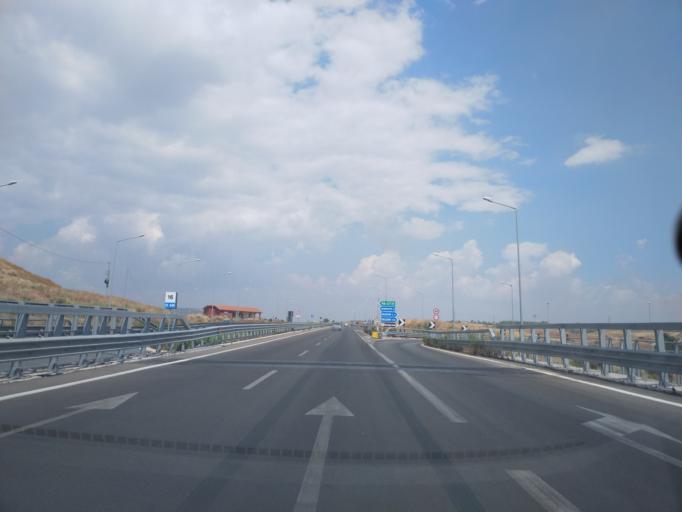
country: IT
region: Sicily
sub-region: Agrigento
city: Favara
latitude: 37.3457
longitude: 13.6507
